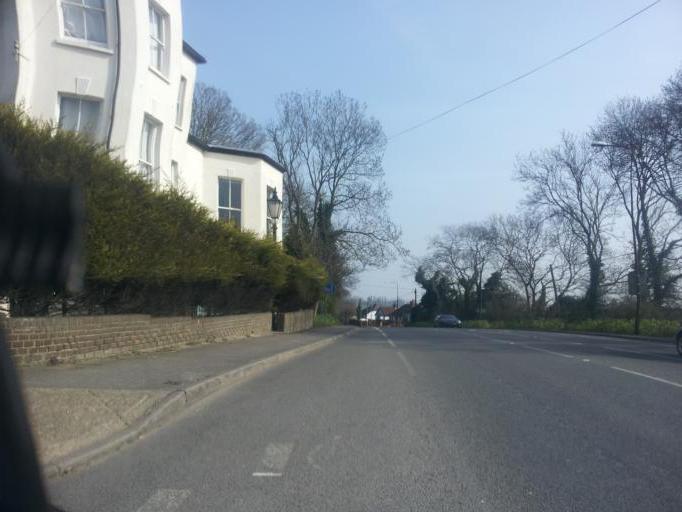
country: GB
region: England
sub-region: Medway
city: Cuxton
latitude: 51.4110
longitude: 0.4589
